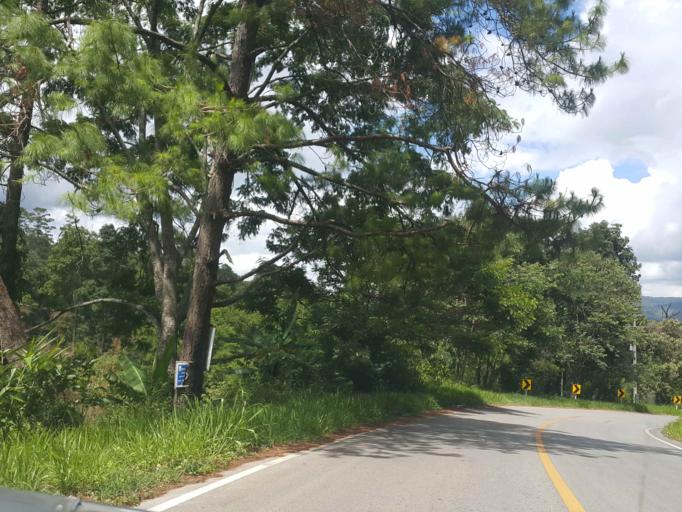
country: TH
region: Chiang Mai
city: Samoeng
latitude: 18.8784
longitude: 98.7879
